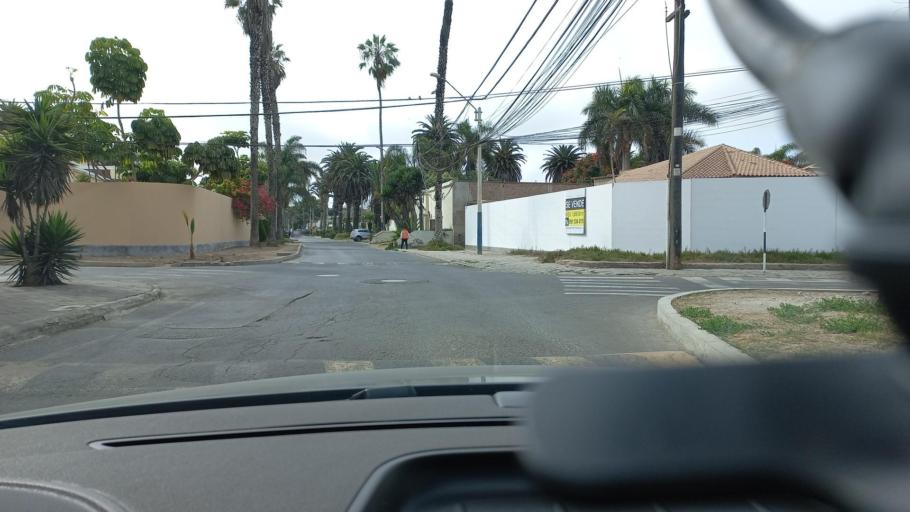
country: PE
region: Lima
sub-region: Lima
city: Surco
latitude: -12.2090
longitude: -77.0062
